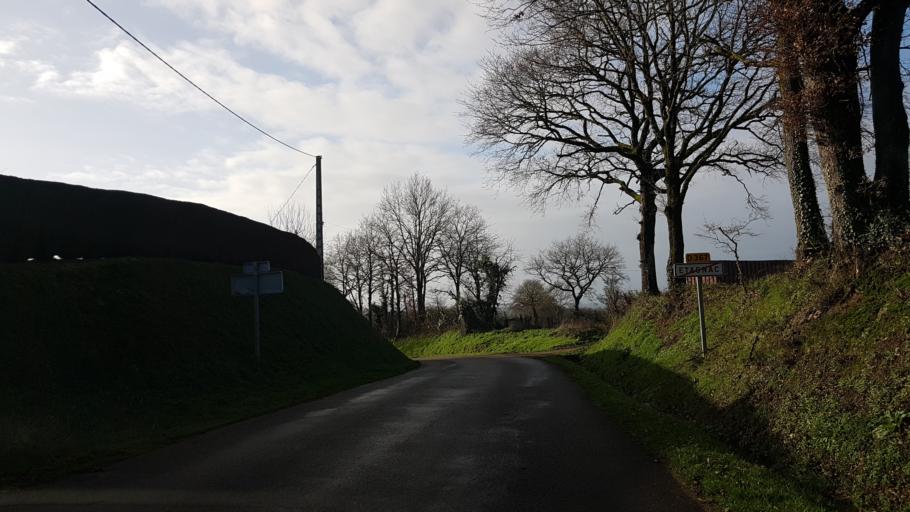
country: FR
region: Poitou-Charentes
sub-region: Departement de la Charente
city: Etagnac
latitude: 45.8930
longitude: 0.7759
